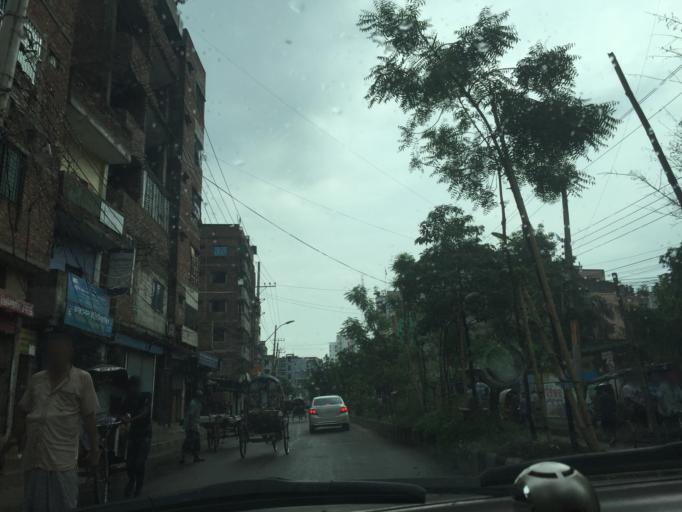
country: BD
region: Dhaka
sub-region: Dhaka
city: Dhaka
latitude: 23.7080
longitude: 90.4201
